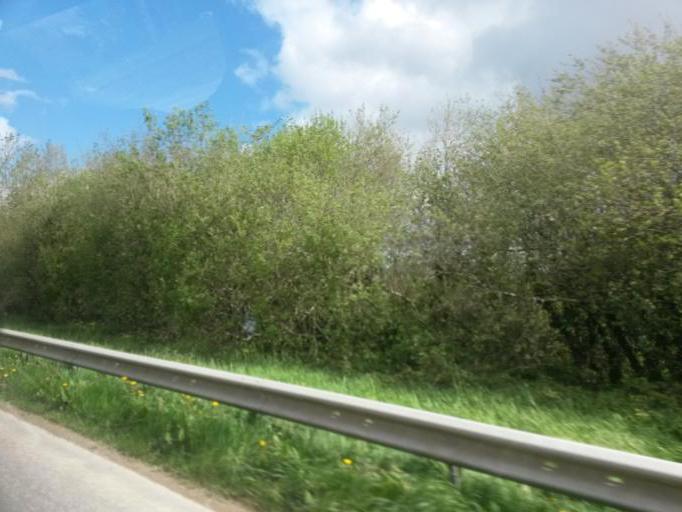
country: IE
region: Leinster
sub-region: Loch Garman
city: Enniscorthy
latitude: 52.4527
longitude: -6.5534
